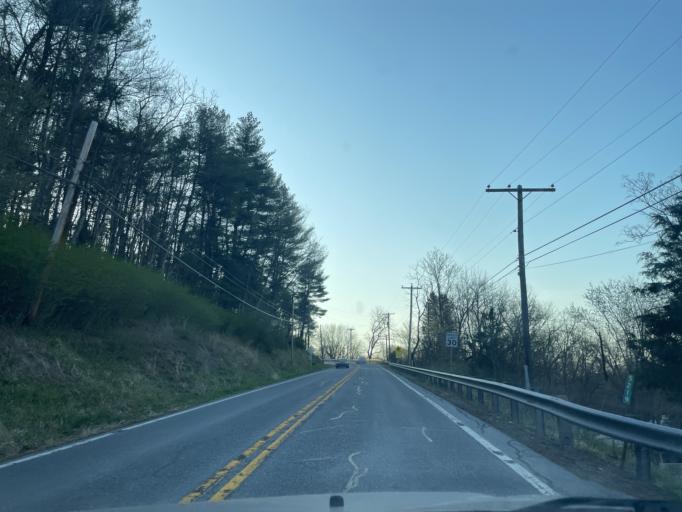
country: US
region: Maryland
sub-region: Washington County
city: Hancock
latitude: 39.6981
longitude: -78.2007
